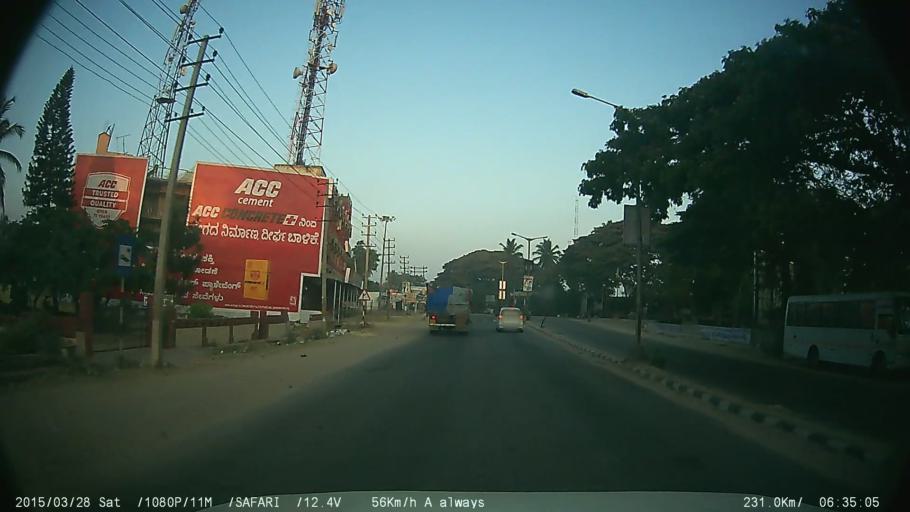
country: IN
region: Karnataka
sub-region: Ramanagara
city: Channapatna
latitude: 12.6531
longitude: 77.2018
